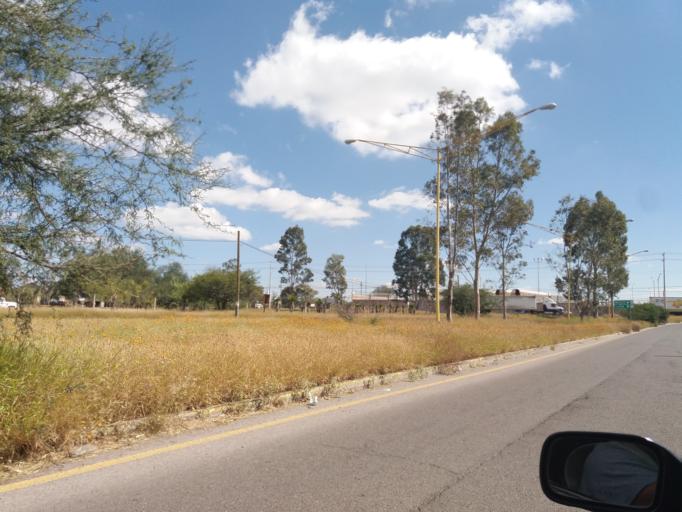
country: MX
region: Aguascalientes
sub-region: Aguascalientes
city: San Sebastian [Fraccionamiento]
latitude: 21.8194
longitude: -102.2879
